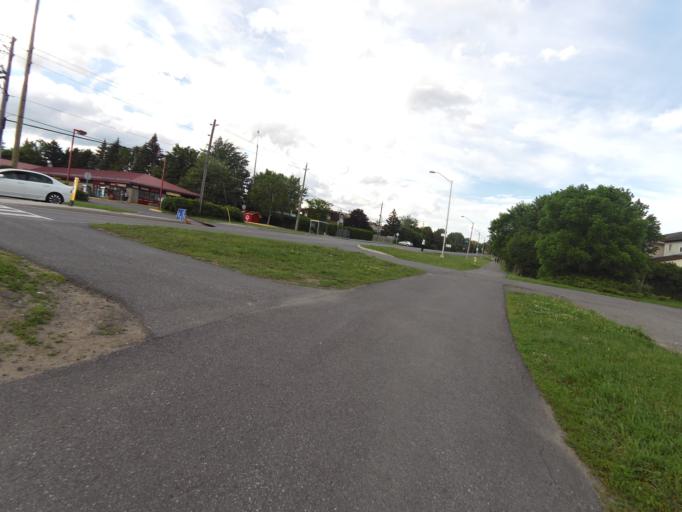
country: CA
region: Ontario
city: Bells Corners
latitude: 45.2749
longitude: -75.7773
